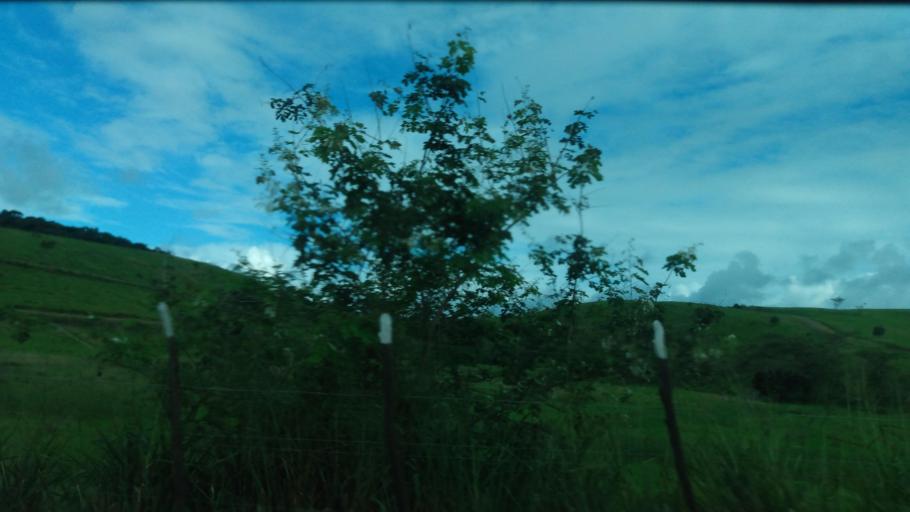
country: BR
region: Pernambuco
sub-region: Catende
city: Catende
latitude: -8.7081
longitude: -35.7622
